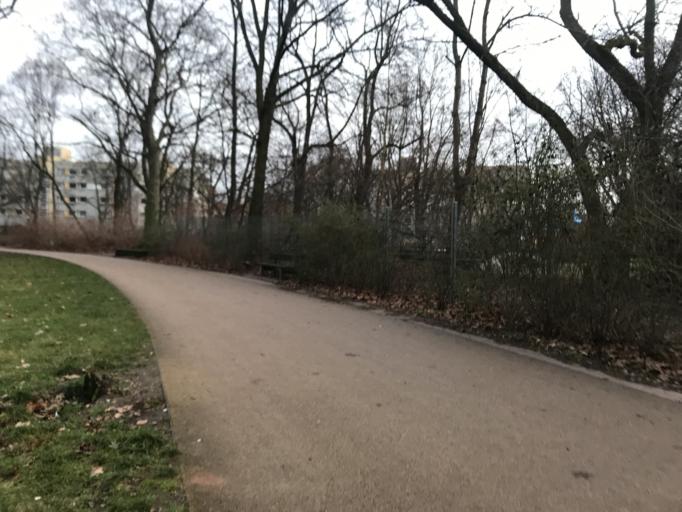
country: DE
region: Berlin
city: Tiergarten Bezirk
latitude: 52.5268
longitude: 13.3566
